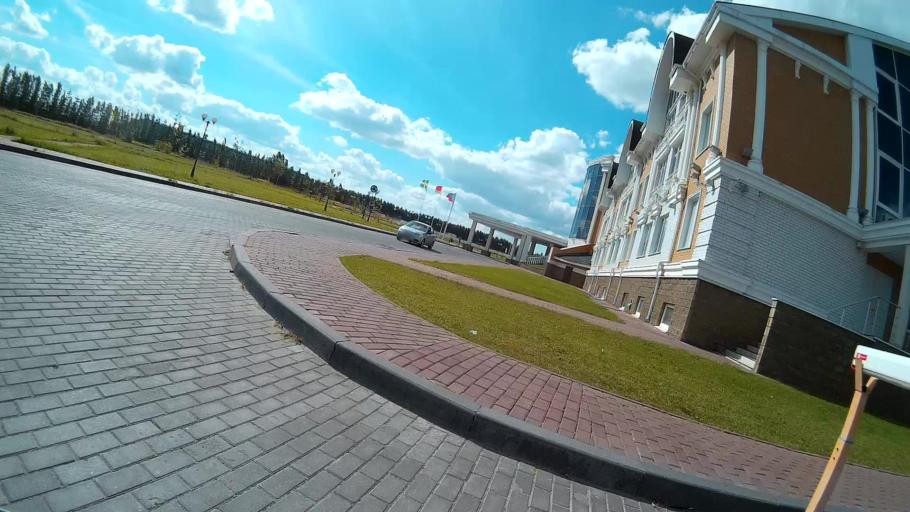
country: RU
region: Ulyanovsk
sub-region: Ulyanovskiy Rayon
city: Ulyanovsk
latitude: 54.2727
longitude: 48.2661
